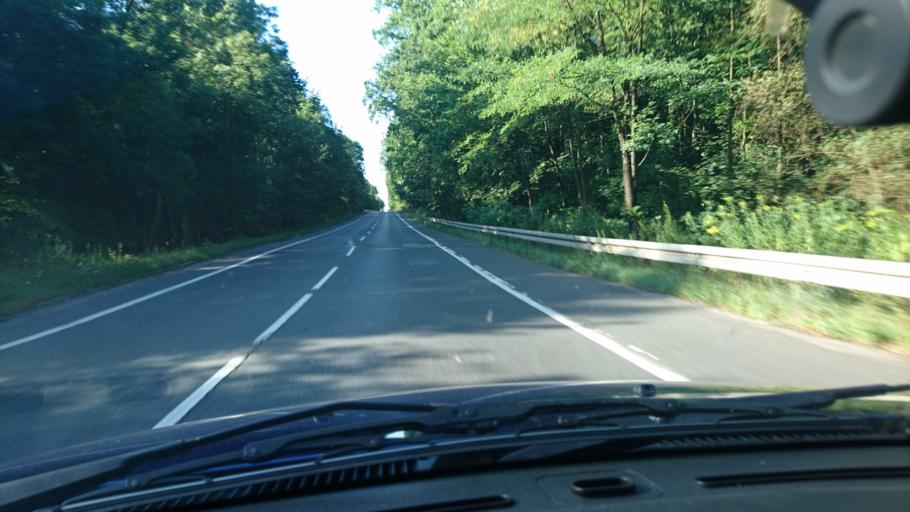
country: PL
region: Silesian Voivodeship
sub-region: Gliwice
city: Gliwice
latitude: 50.3443
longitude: 18.6504
